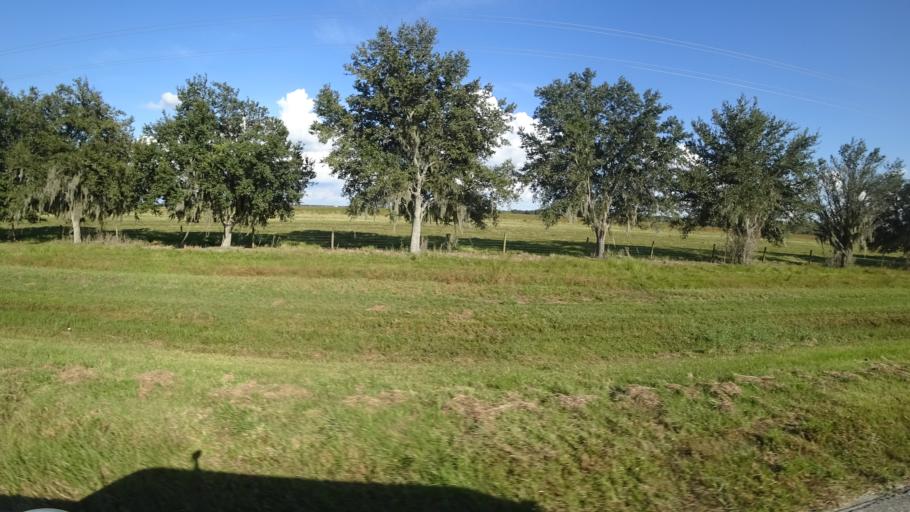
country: US
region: Florida
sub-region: Sarasota County
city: The Meadows
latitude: 27.4194
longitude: -82.3037
